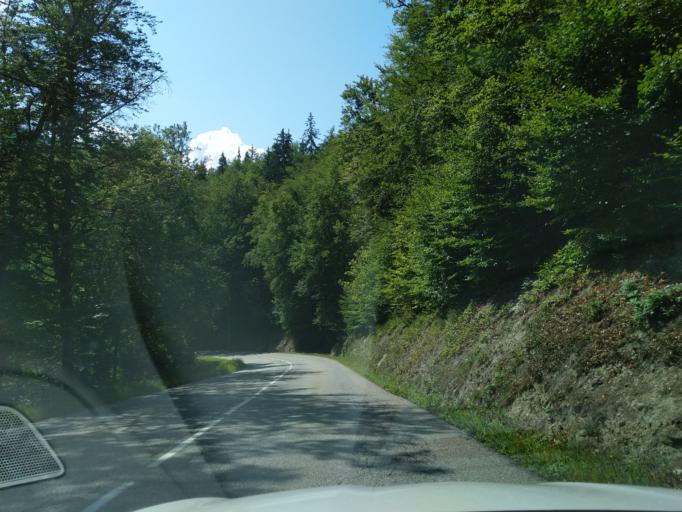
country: FR
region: Rhone-Alpes
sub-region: Departement de la Savoie
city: Les Allues
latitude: 45.4492
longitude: 6.5613
